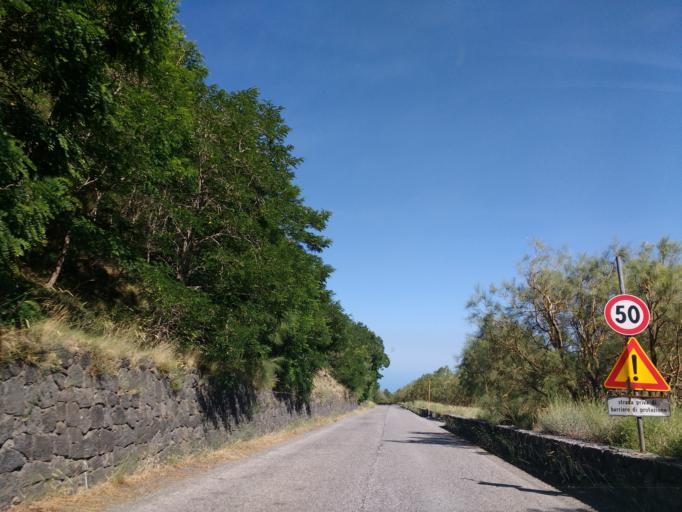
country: IT
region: Sicily
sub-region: Catania
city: Nicolosi
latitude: 37.6994
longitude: 15.0173
